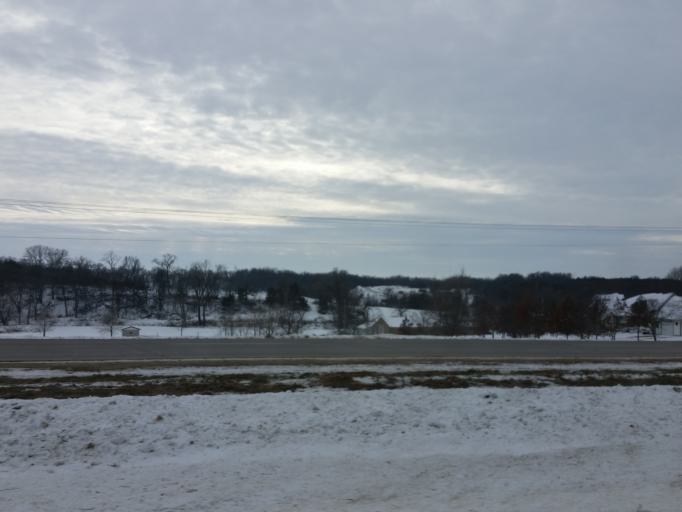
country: US
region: Iowa
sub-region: Dubuque County
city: Dyersville
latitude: 42.4696
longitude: -91.0931
